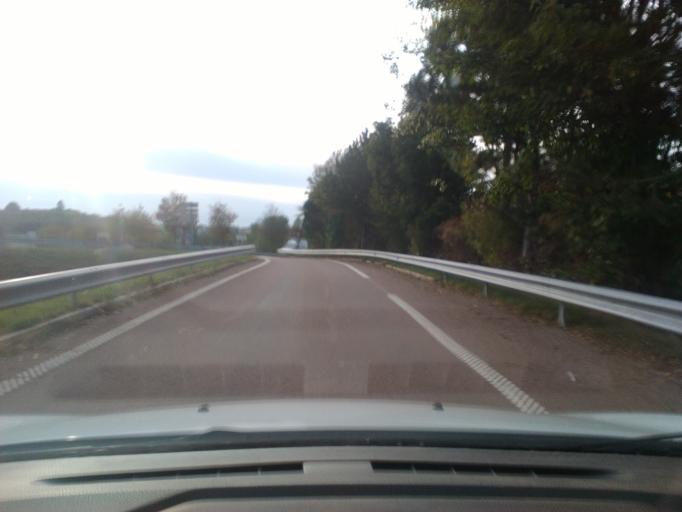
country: FR
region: Lorraine
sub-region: Departement des Vosges
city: Darnieulles
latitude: 48.2201
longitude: 6.2447
